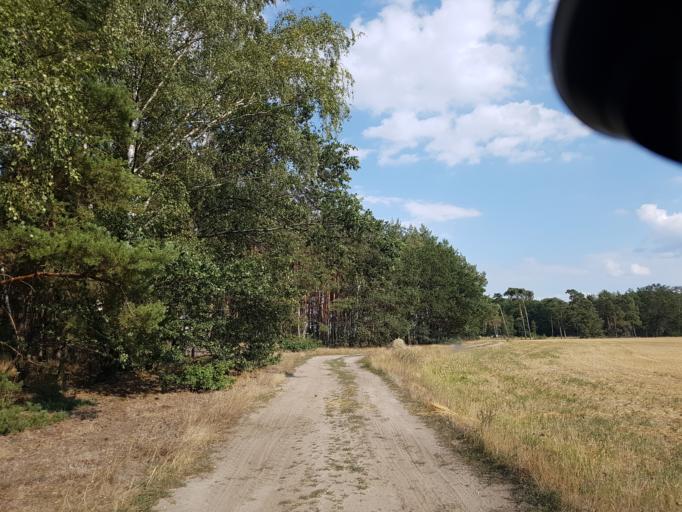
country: DE
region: Brandenburg
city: Calau
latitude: 51.7648
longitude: 13.9587
